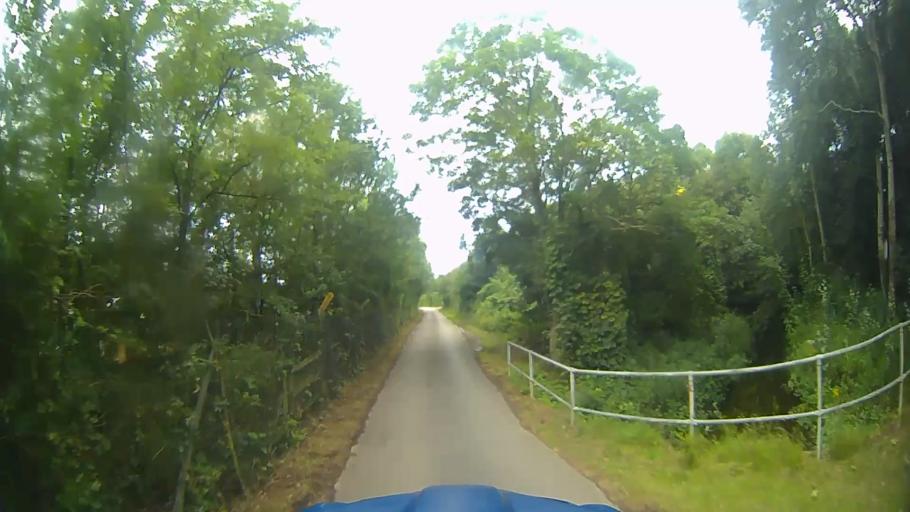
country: GB
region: England
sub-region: Wokingham
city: Woodley
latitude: 51.4395
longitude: -0.8776
